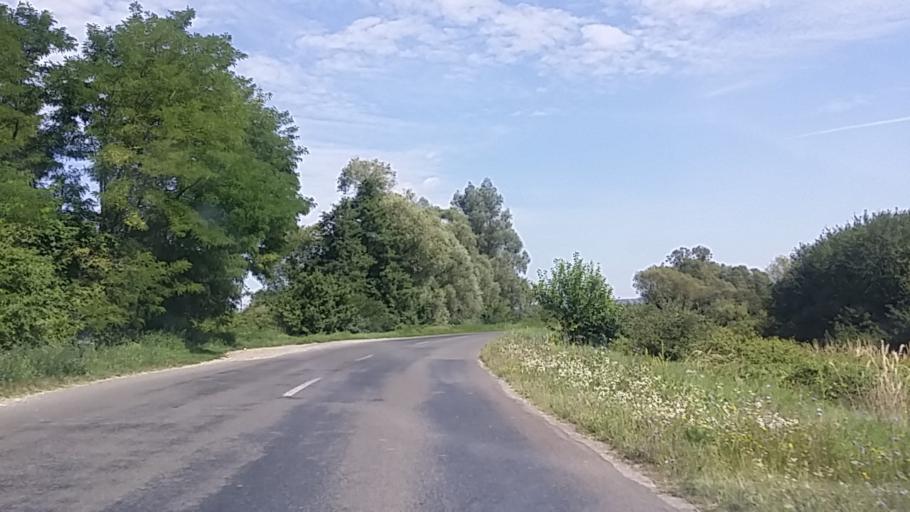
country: HU
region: Baranya
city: Sasd
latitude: 46.2138
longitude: 18.1044
